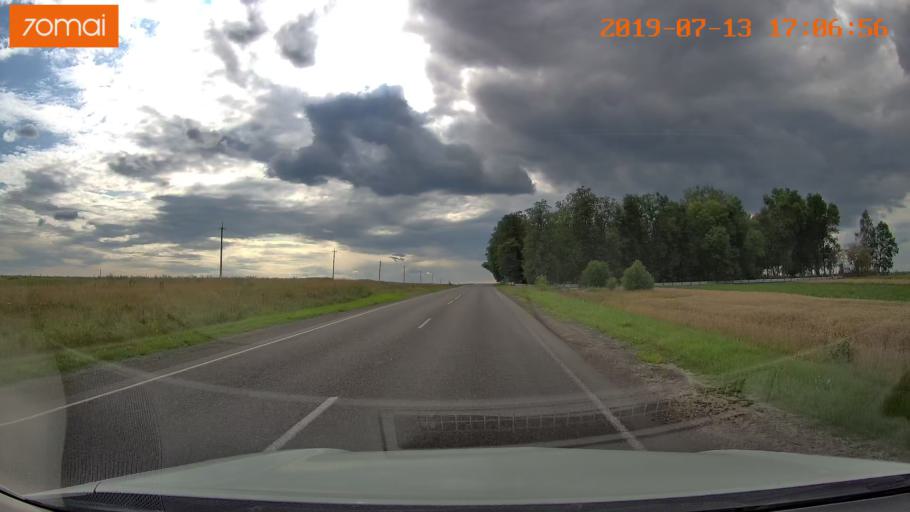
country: BY
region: Mogilev
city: Kirawsk
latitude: 53.2679
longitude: 29.3423
